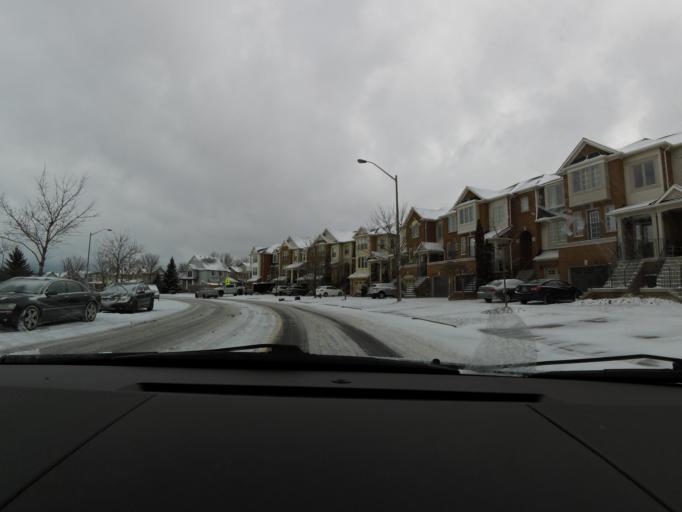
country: CA
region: Ontario
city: Burlington
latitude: 43.4013
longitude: -79.7966
